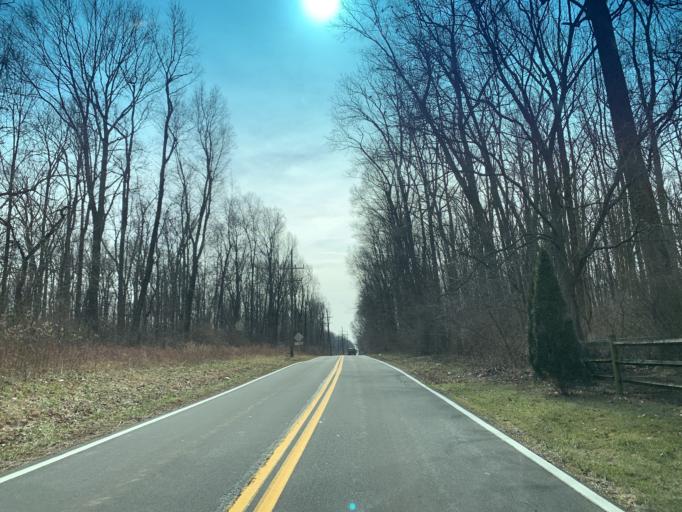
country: US
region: Maryland
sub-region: Frederick County
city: Buckeystown
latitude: 39.3296
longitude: -77.4554
